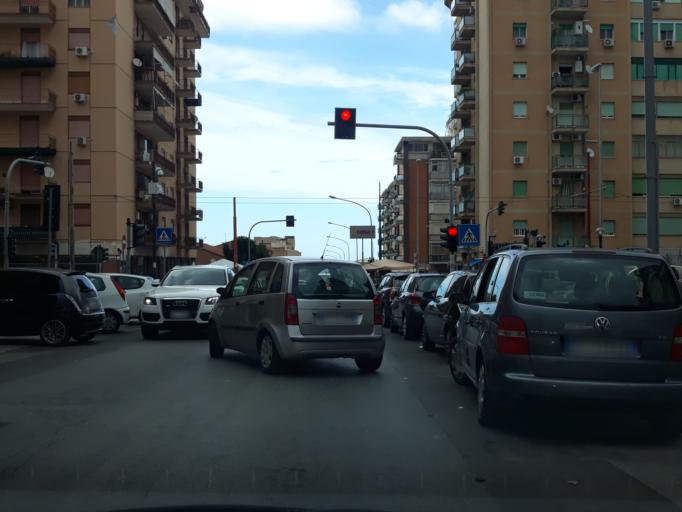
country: IT
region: Sicily
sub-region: Palermo
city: Ciaculli
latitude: 38.1001
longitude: 13.3927
